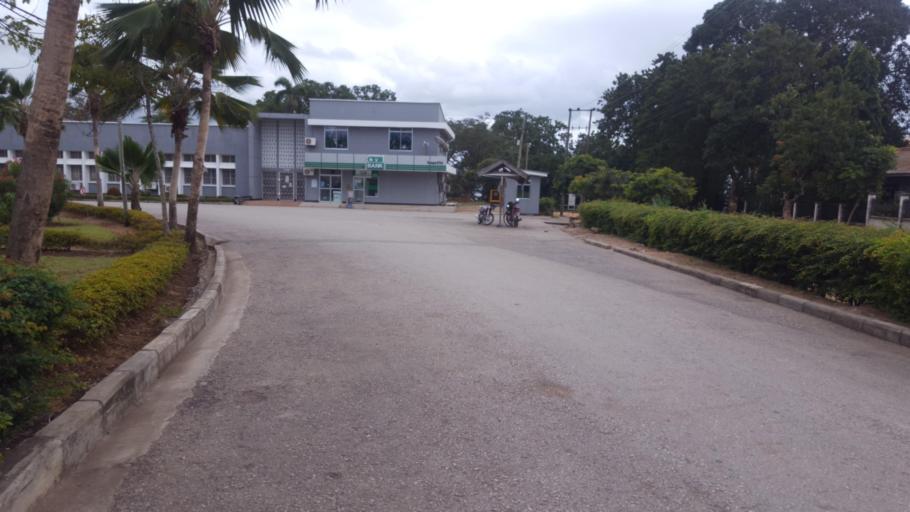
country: TZ
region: Tanga
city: Tanga
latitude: -5.0698
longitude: 39.0979
